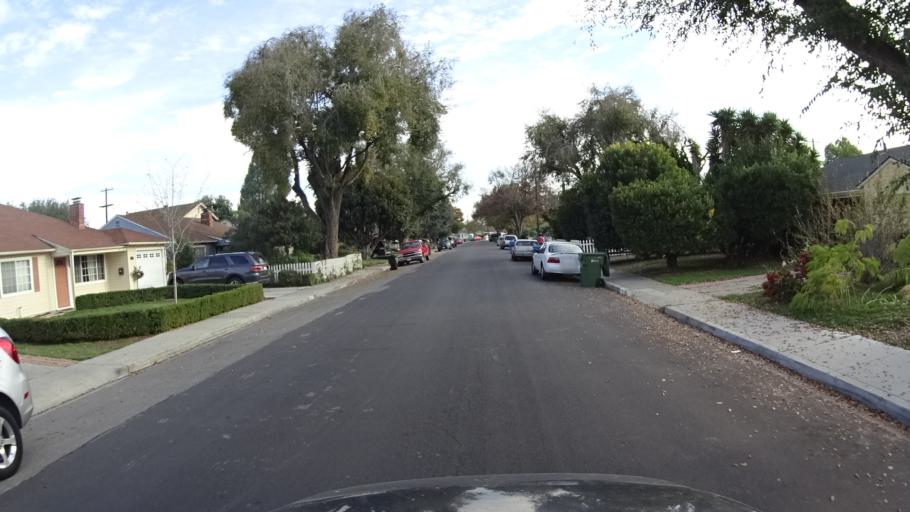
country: US
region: California
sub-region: Santa Clara County
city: Santa Clara
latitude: 37.3401
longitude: -121.9590
